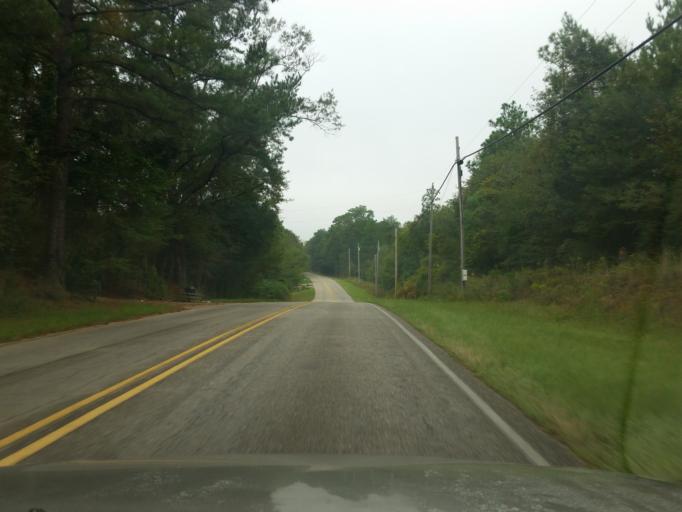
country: US
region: Alabama
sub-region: Baldwin County
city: Bay Minette
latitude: 30.8516
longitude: -87.8163
